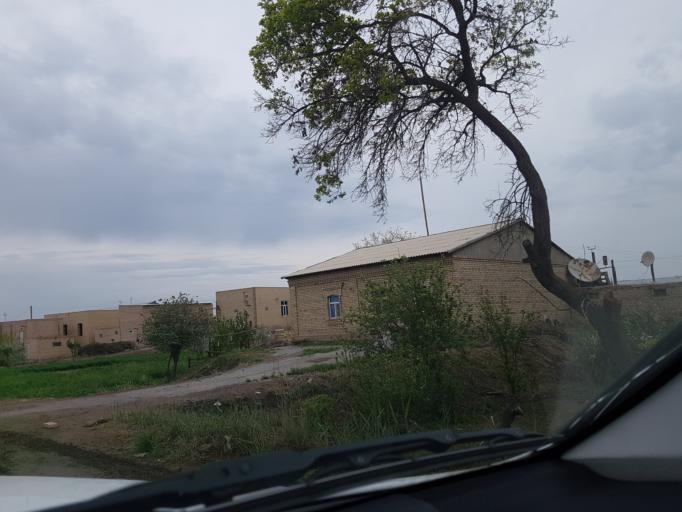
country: TM
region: Lebap
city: Turkmenabat
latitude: 39.0659
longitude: 63.5643
